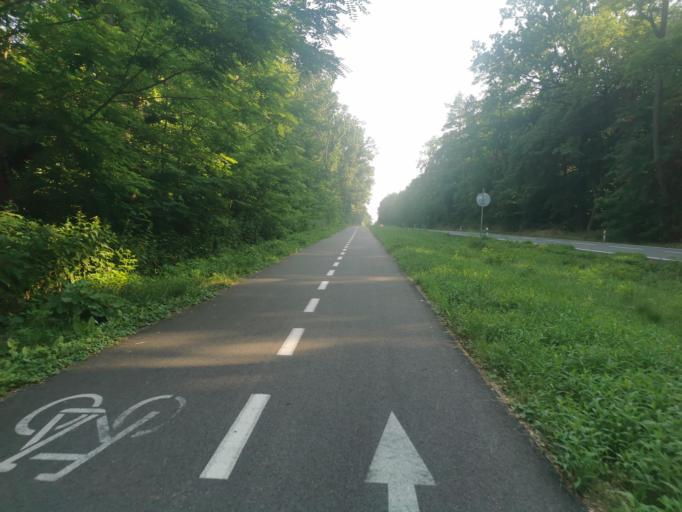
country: CZ
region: South Moravian
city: Ratiskovice
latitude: 48.9054
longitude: 17.1610
